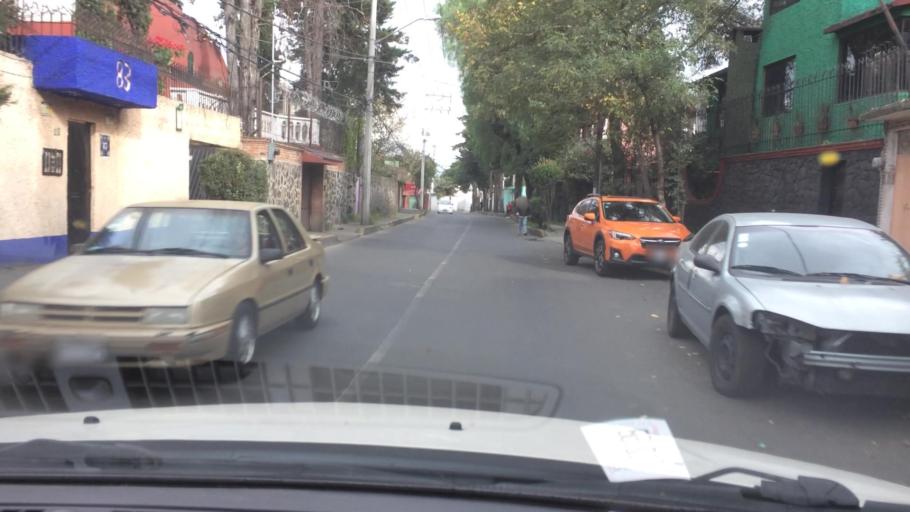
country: MX
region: Mexico City
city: Xochimilco
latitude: 19.2664
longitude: -99.1299
